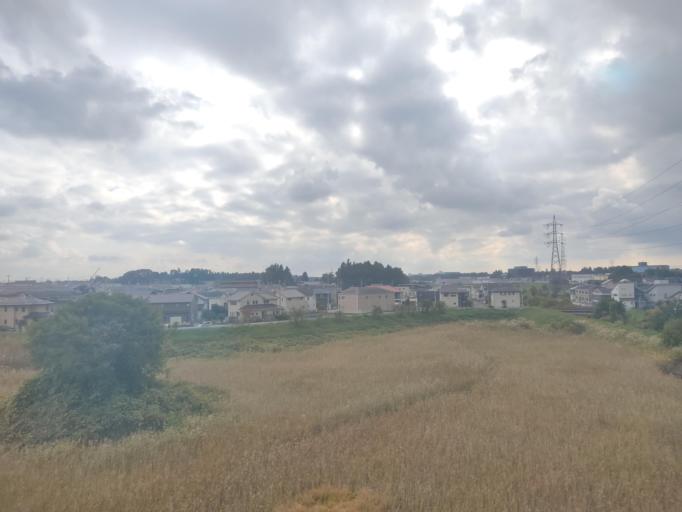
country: JP
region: Ibaraki
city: Naka
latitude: 36.0811
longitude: 140.0924
